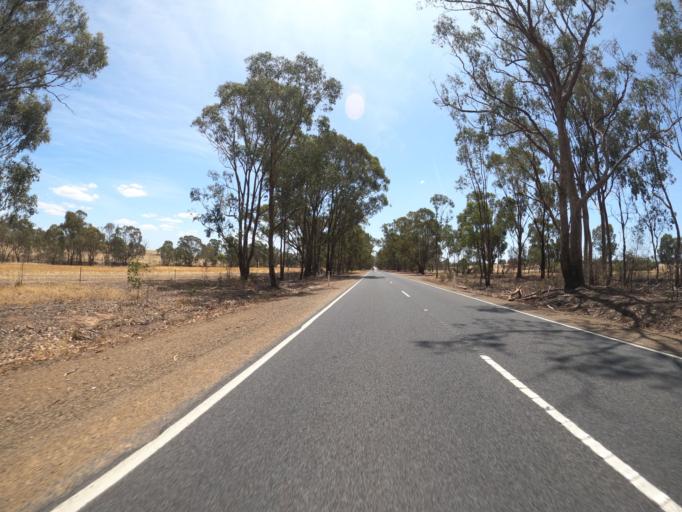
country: AU
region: Victoria
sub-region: Benalla
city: Benalla
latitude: -36.3695
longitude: 145.9717
